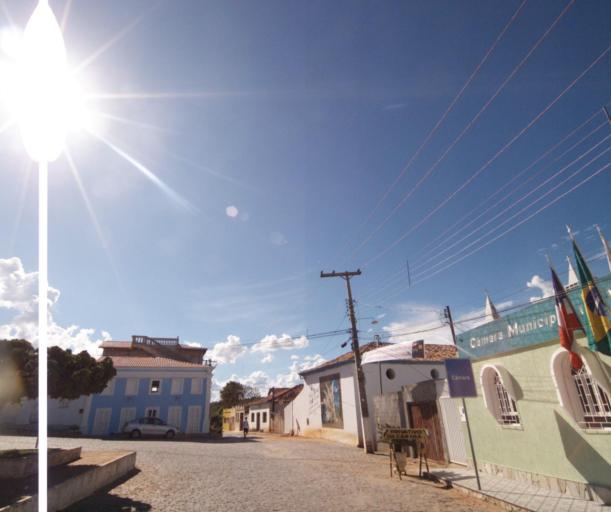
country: BR
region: Bahia
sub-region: Correntina
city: Correntina
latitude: -13.3419
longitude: -44.6372
